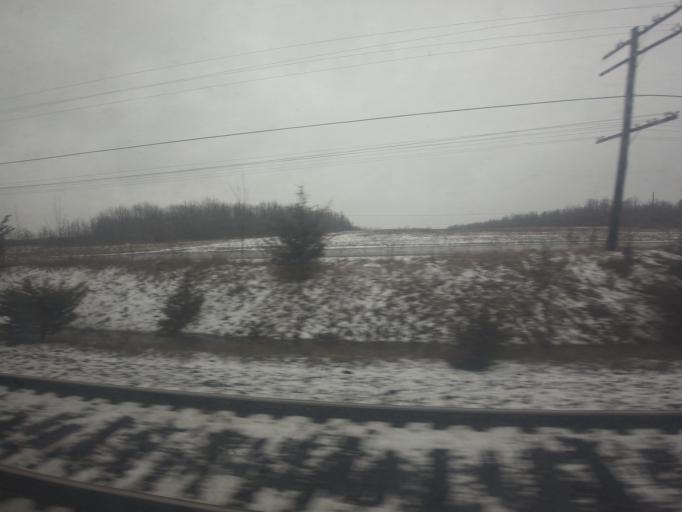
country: CA
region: Ontario
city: Belleville
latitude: 44.1572
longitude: -77.4540
